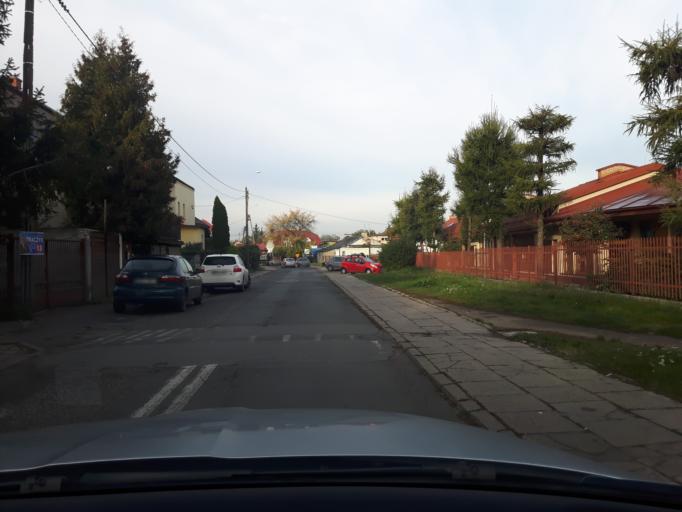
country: PL
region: Masovian Voivodeship
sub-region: Powiat wolominski
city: Zabki
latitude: 52.2853
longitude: 21.1113
